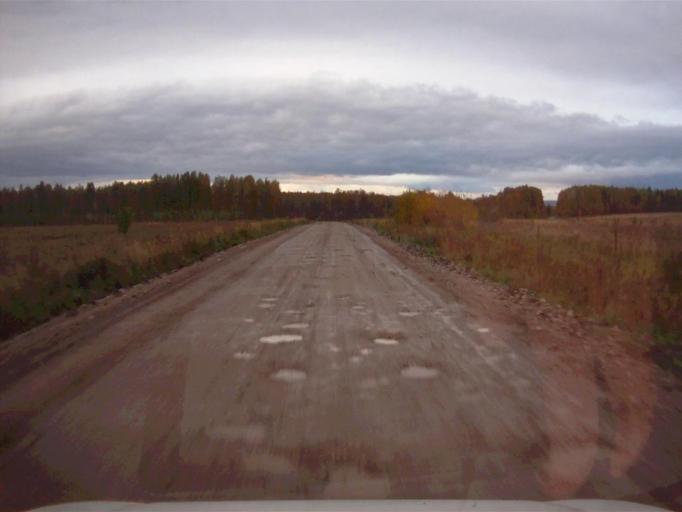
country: RU
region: Sverdlovsk
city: Mikhaylovsk
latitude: 56.1889
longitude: 59.1879
